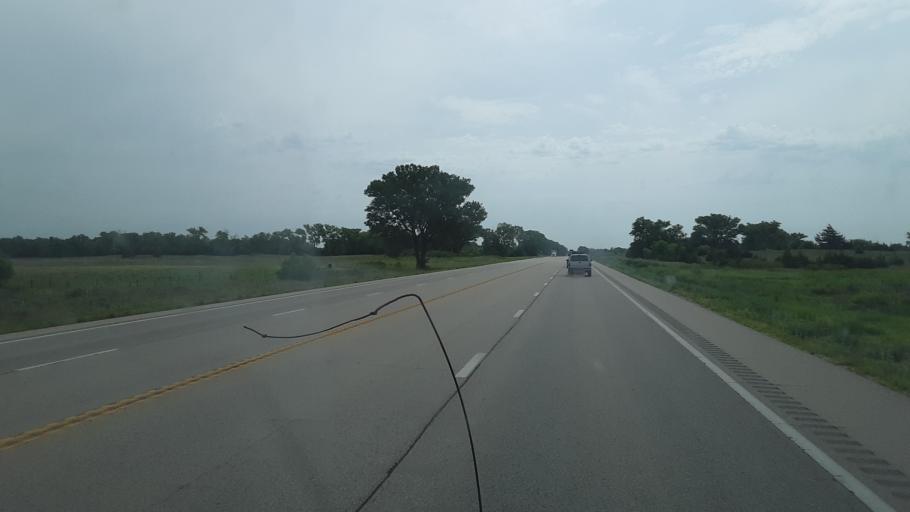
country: US
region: Kansas
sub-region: Rice County
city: Sterling
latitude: 37.9846
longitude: -98.2940
